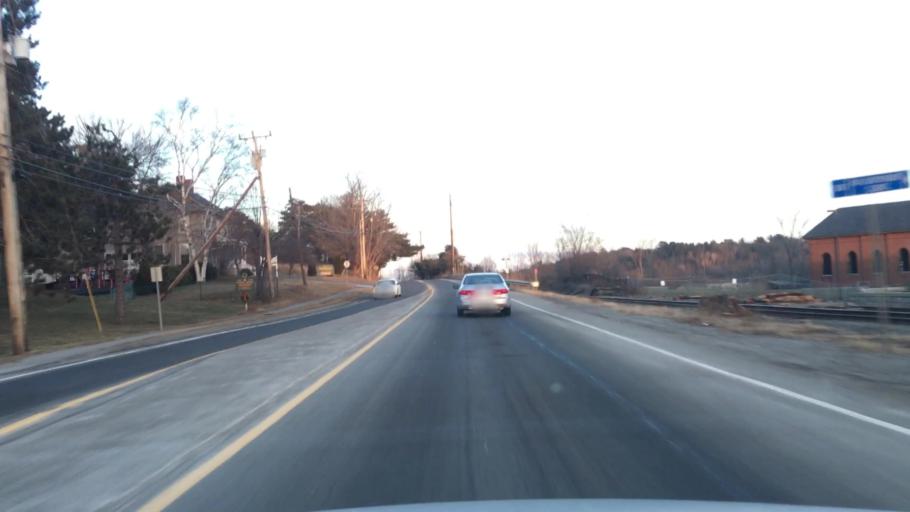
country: US
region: Maine
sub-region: Penobscot County
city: Brewer
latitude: 44.8118
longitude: -68.7430
